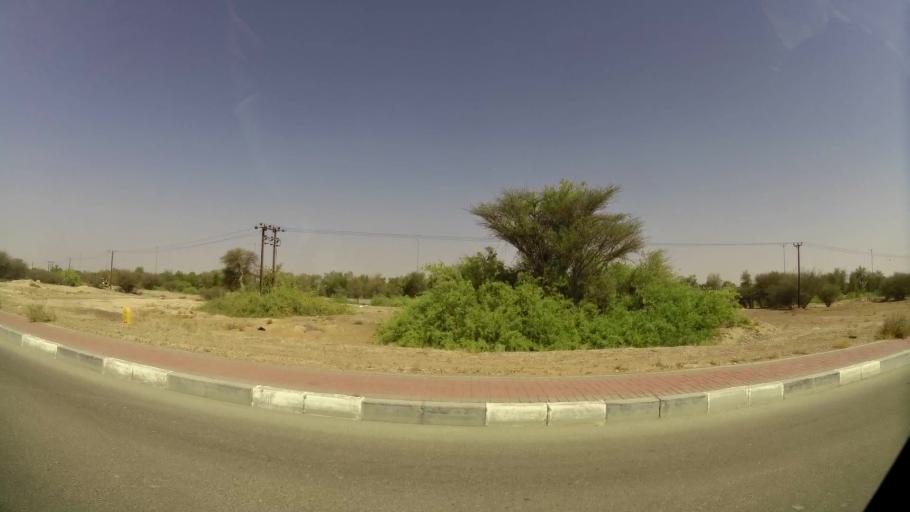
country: OM
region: Al Buraimi
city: Al Buraymi
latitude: 24.3012
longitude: 55.7926
